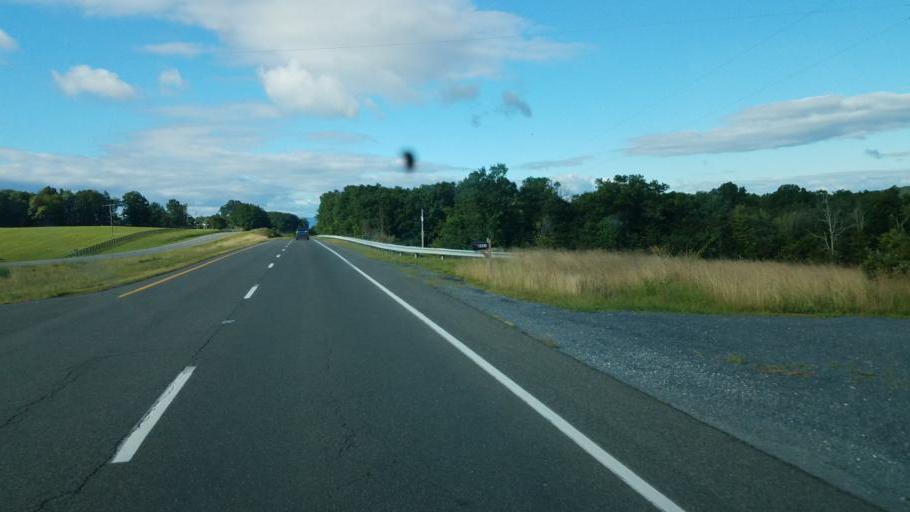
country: US
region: Virginia
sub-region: Frederick County
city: Shawnee Land
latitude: 39.3741
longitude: -78.2959
